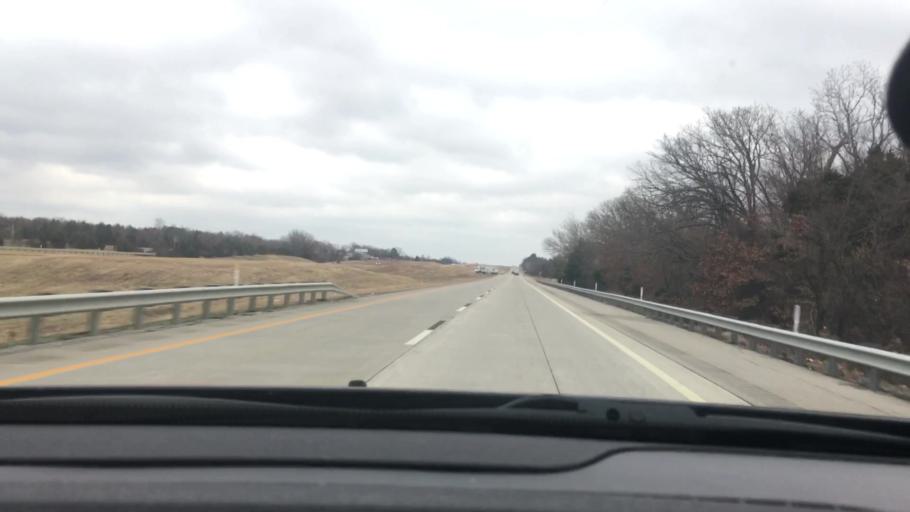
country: US
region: Oklahoma
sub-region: Bryan County
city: Durant
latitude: 34.1822
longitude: -96.2469
